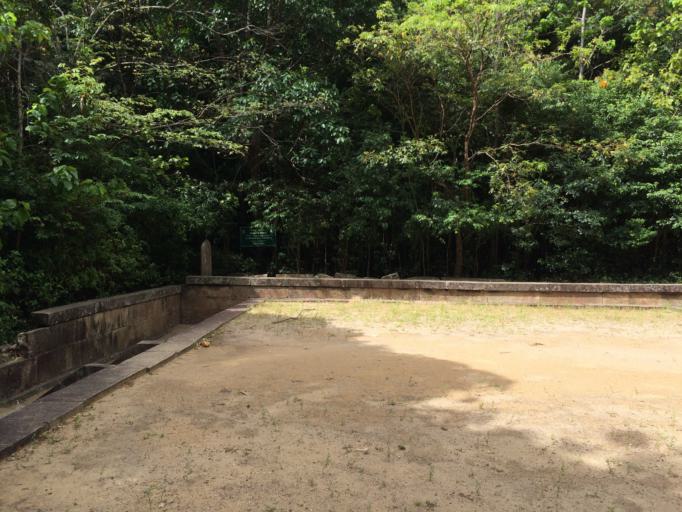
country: LK
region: Central
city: Sigiriya
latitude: 8.1189
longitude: 80.6613
